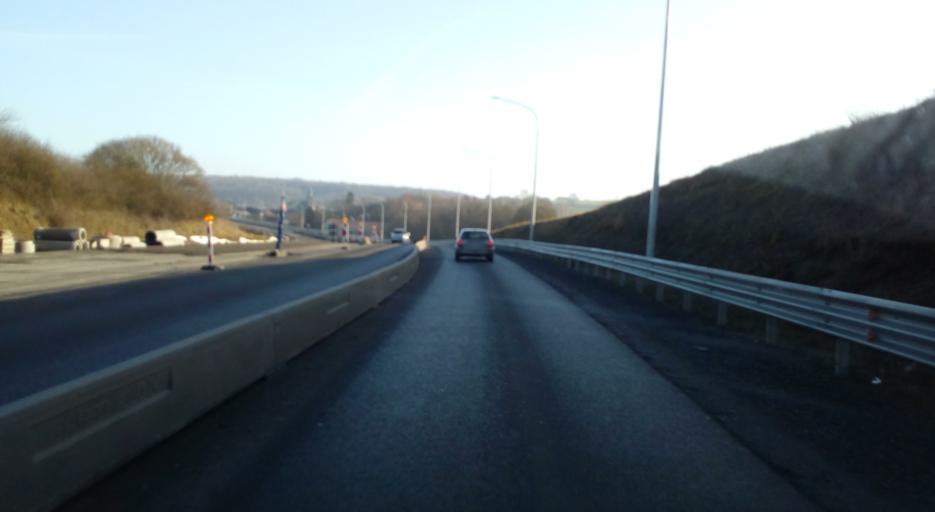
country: BE
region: Wallonia
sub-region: Province de Namur
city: Walcourt
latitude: 50.2807
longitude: 4.4855
